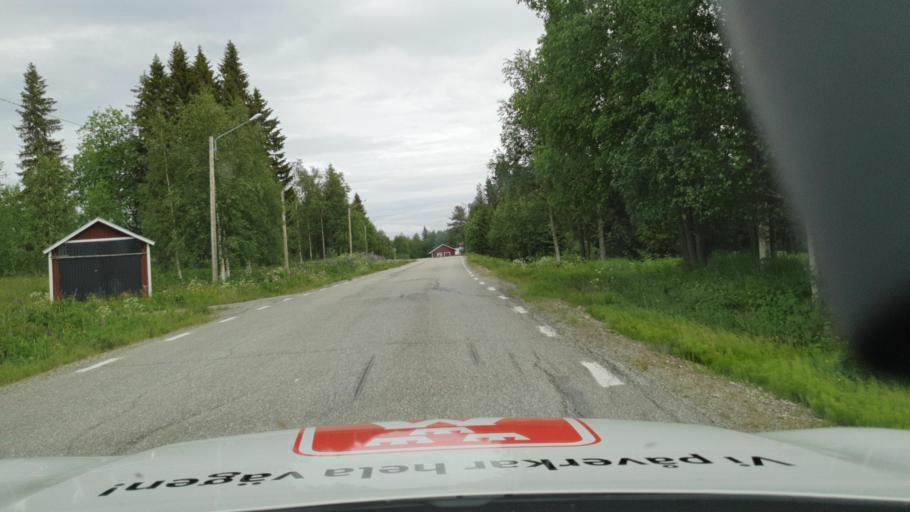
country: SE
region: Vaesterbotten
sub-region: Lycksele Kommun
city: Soderfors
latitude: 64.3618
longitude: 18.1020
